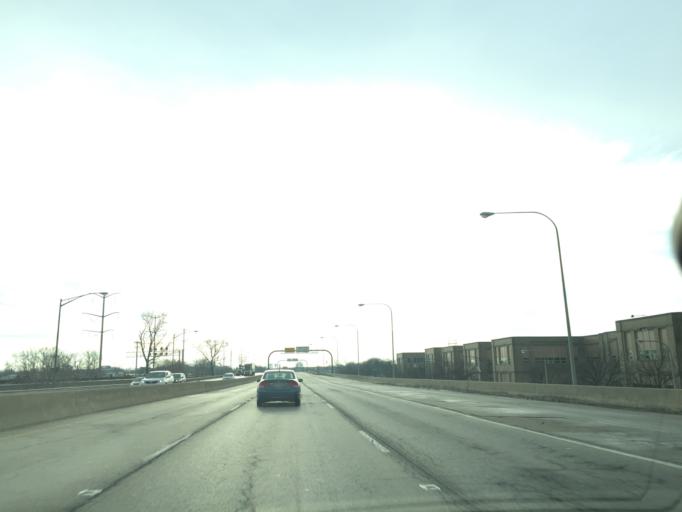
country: US
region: Indiana
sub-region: Lake County
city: Whiting
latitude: 41.7403
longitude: -87.5728
